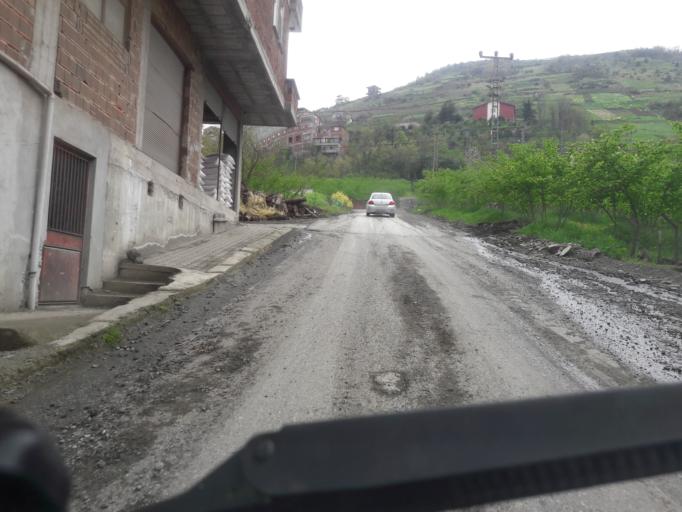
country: TR
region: Trabzon
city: Derecik
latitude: 40.9443
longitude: 39.5000
